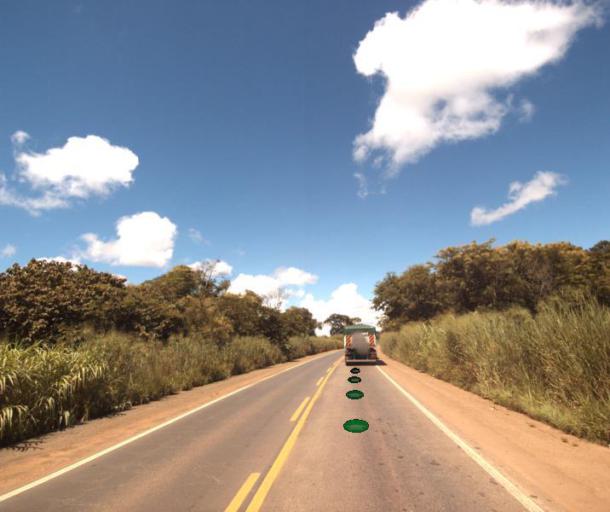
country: BR
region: Goias
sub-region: Anapolis
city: Anapolis
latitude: -16.1551
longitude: -49.0438
